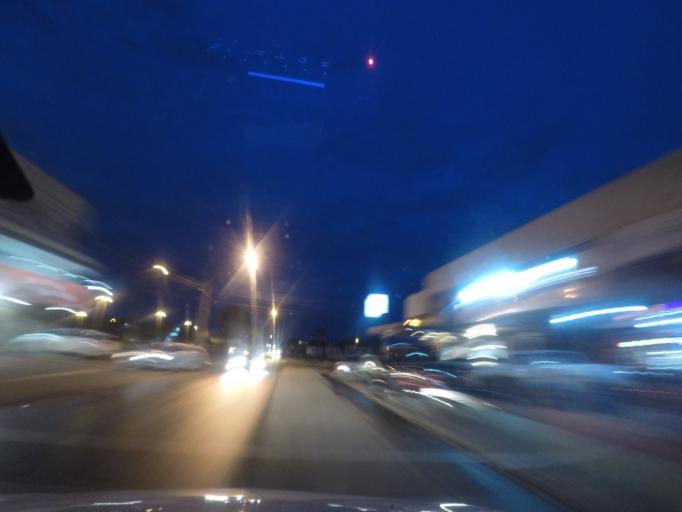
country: BR
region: Goias
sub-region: Goiania
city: Goiania
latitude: -16.7062
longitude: -49.3245
